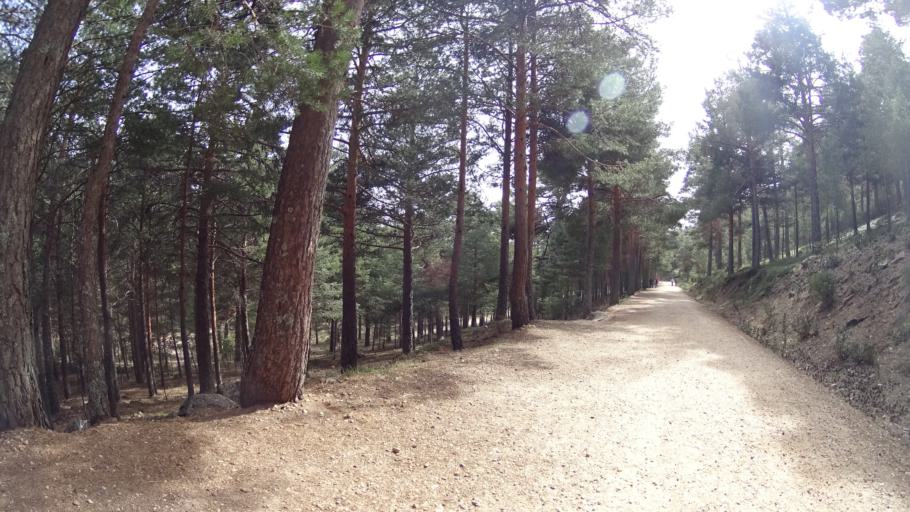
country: ES
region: Madrid
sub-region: Provincia de Madrid
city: Navacerrada
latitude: 40.7628
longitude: -3.9961
